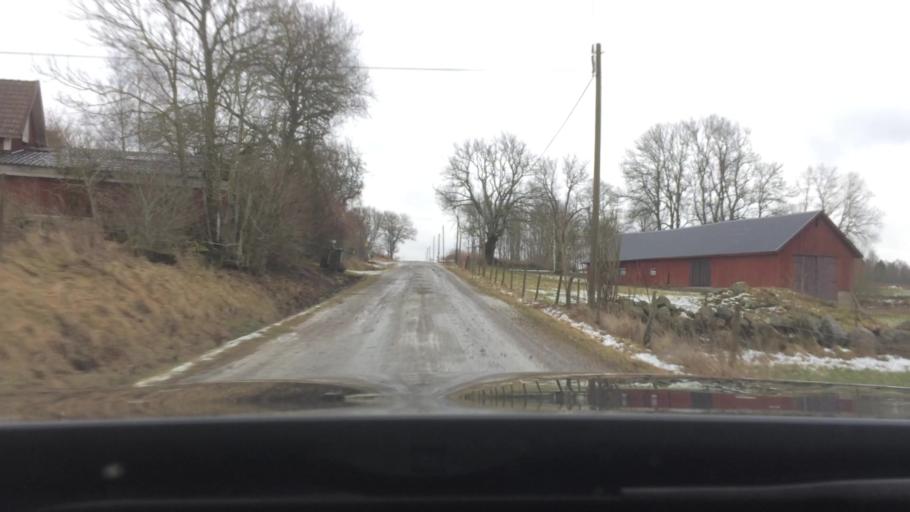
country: SE
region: Vaestra Goetaland
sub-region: Falkopings Kommun
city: Floby
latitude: 57.9959
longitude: 13.3959
